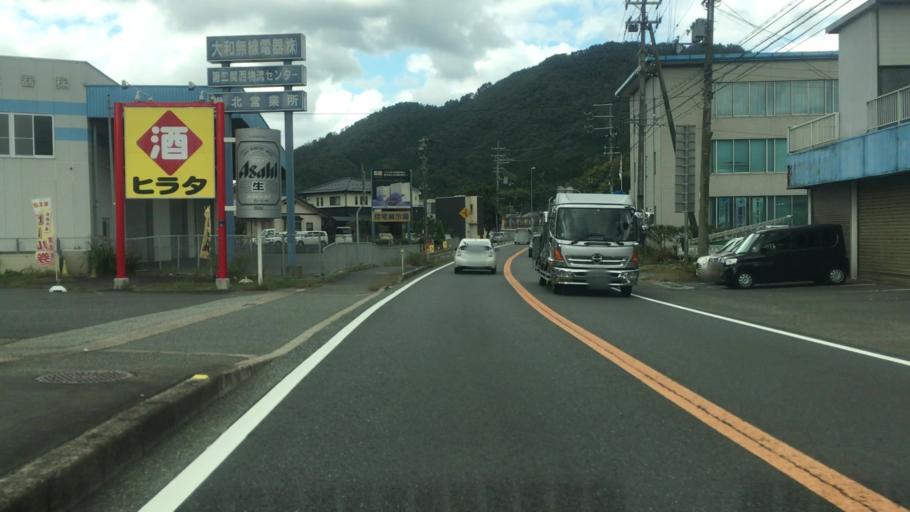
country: JP
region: Hyogo
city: Toyooka
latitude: 35.3223
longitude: 134.8783
